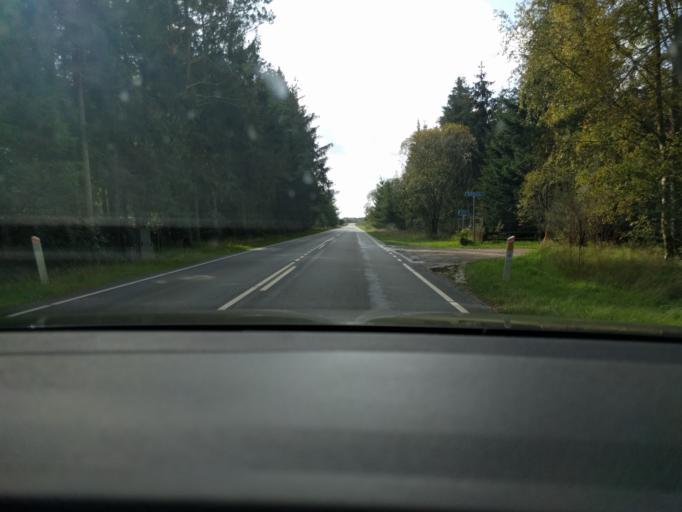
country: DK
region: Central Jutland
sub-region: Viborg Kommune
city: Bjerringbro
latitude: 56.2838
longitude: 9.6447
